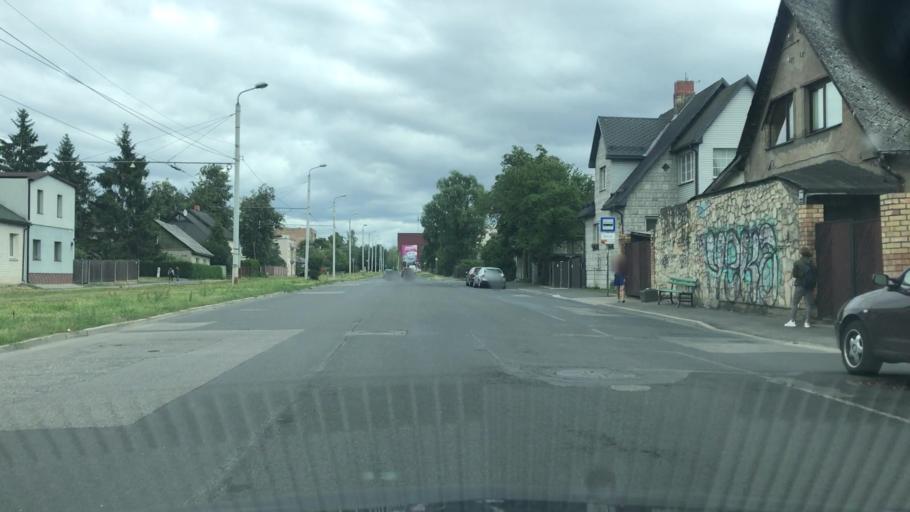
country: LV
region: Marupe
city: Marupe
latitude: 56.9575
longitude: 24.0278
